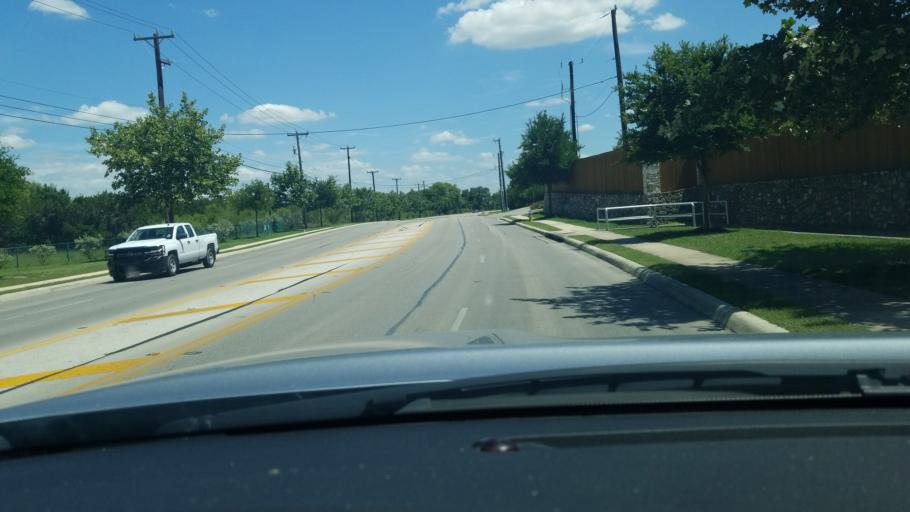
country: US
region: Texas
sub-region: Bexar County
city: Timberwood Park
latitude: 29.6958
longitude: -98.4807
